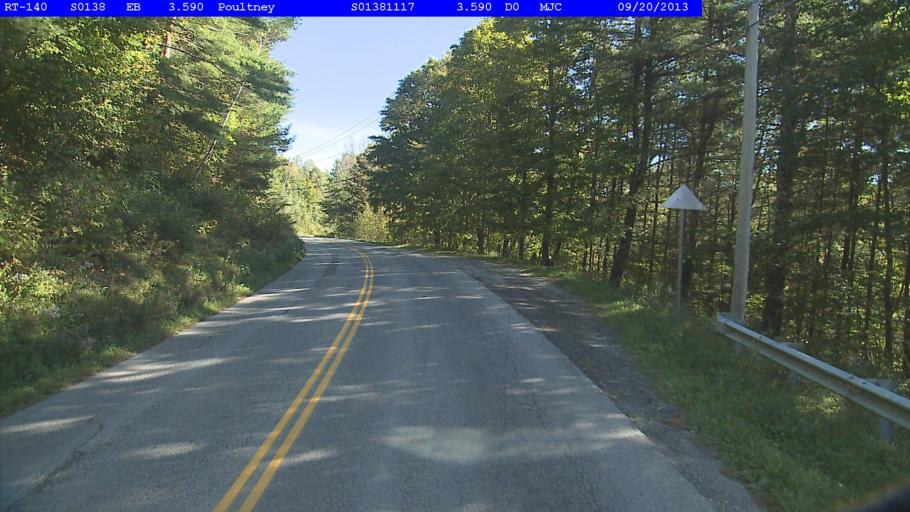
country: US
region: Vermont
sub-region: Rutland County
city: Poultney
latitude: 43.5139
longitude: -73.1779
